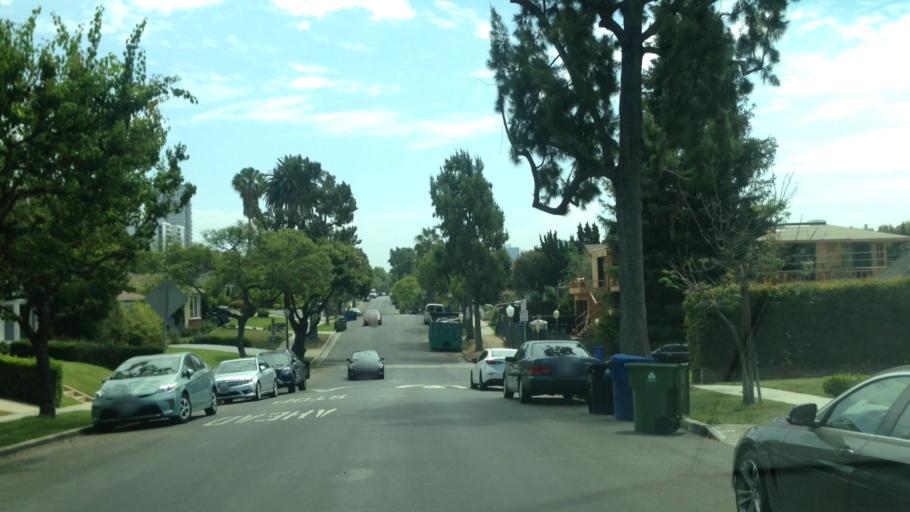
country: US
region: California
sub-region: Los Angeles County
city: Westwood, Los Angeles
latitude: 34.0574
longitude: -118.4412
